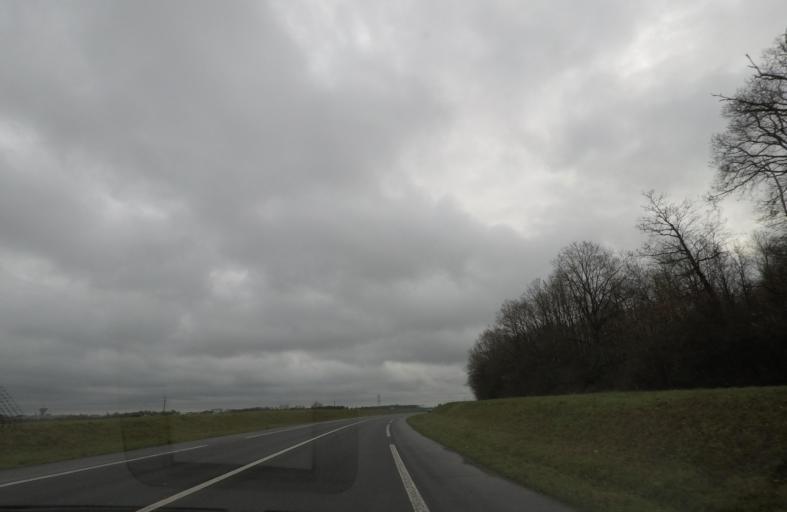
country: FR
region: Centre
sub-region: Departement du Loir-et-Cher
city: Vendome
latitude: 47.7743
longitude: 1.0548
